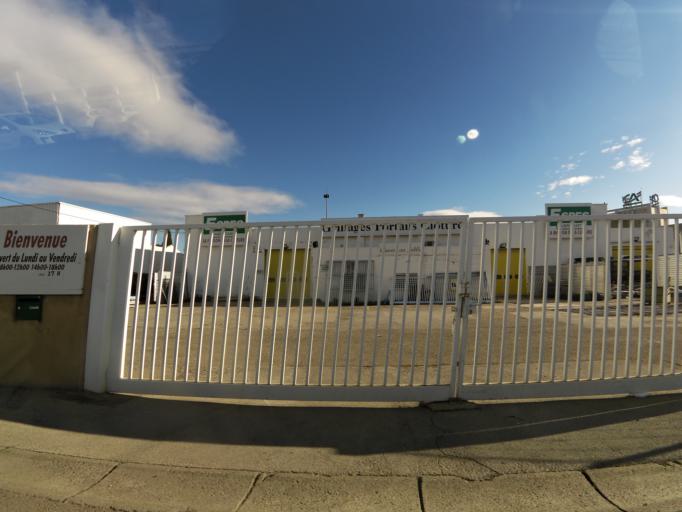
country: FR
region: Languedoc-Roussillon
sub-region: Departement du Gard
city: Milhaud
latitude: 43.8105
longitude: 4.3295
